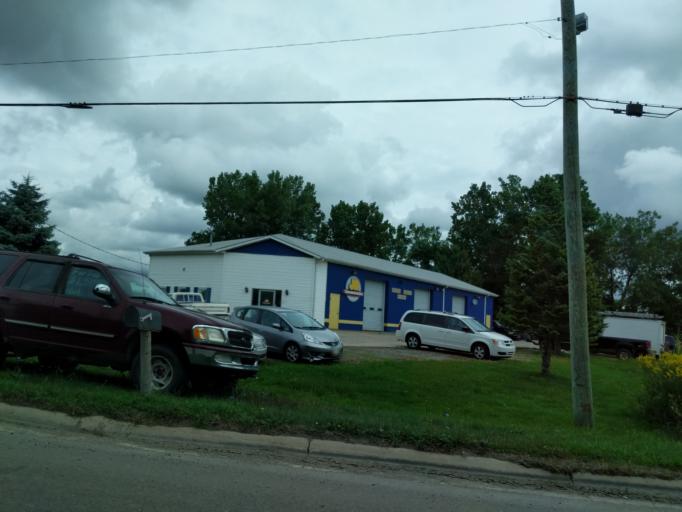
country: US
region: Michigan
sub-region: Lapeer County
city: Almont
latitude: 42.9317
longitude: -83.0536
